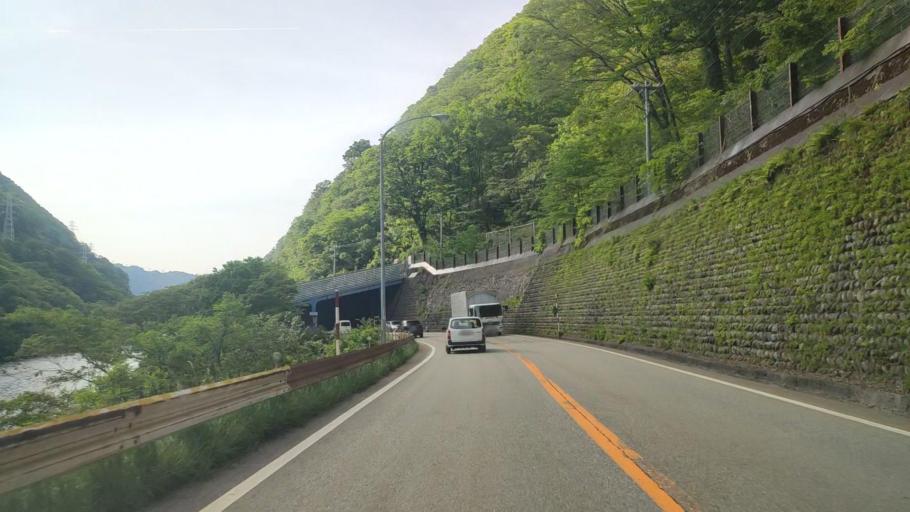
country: JP
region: Toyama
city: Yatsuomachi-higashikumisaka
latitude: 36.4140
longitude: 137.2909
